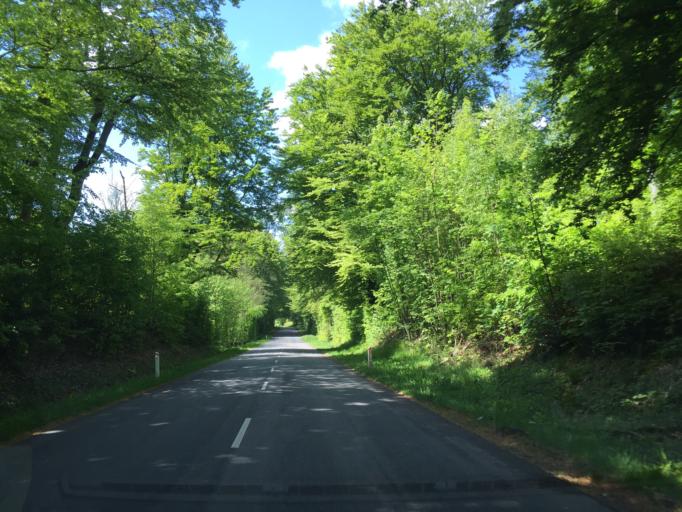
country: DK
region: South Denmark
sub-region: Fredericia Kommune
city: Snoghoj
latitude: 55.5082
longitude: 9.7111
